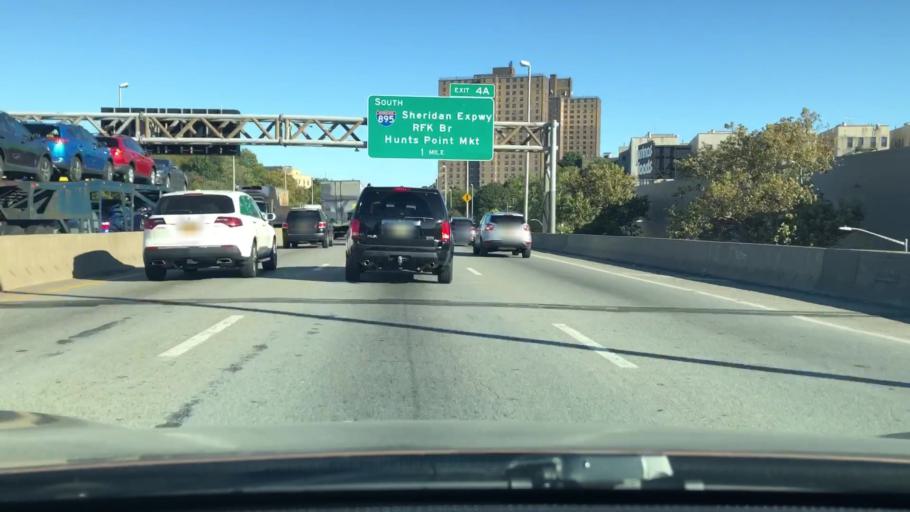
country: US
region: New York
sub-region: Bronx
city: The Bronx
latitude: 40.8441
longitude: -73.8990
